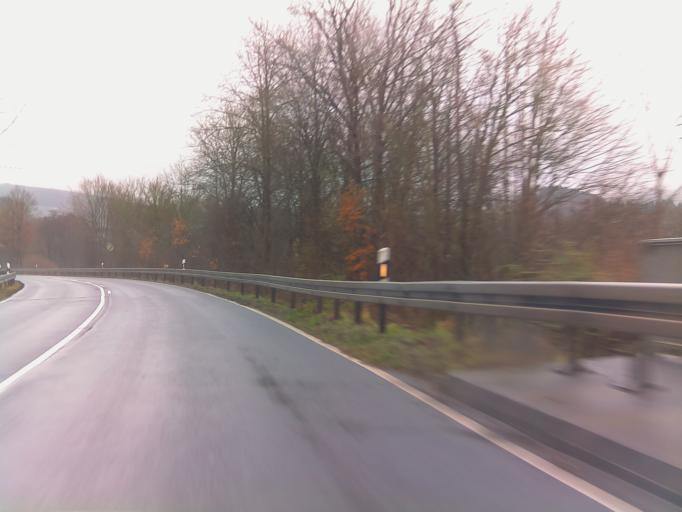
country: DE
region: Hesse
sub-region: Regierungsbezirk Kassel
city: Eichenzell
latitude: 50.4873
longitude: 9.7065
